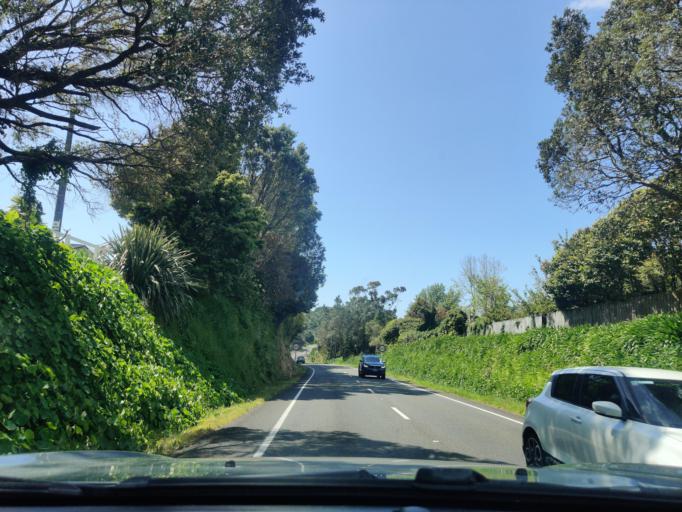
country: NZ
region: Taranaki
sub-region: New Plymouth District
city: New Plymouth
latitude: -39.1148
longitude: 173.9577
